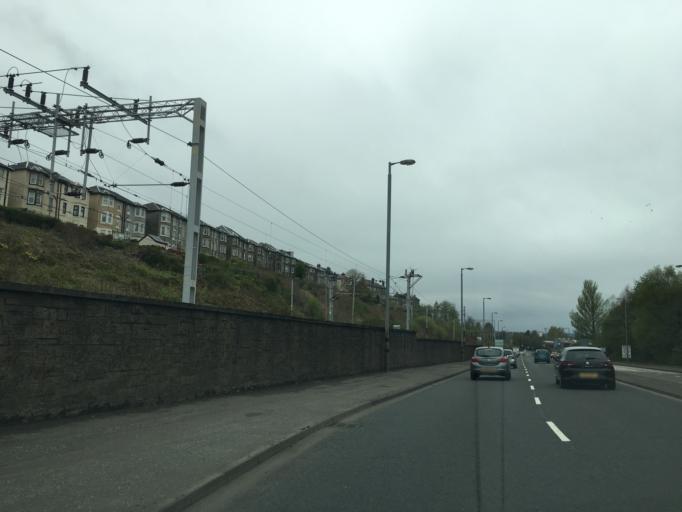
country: GB
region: Scotland
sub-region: Inverclyde
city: Port Glasgow
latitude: 55.9360
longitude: -4.7033
